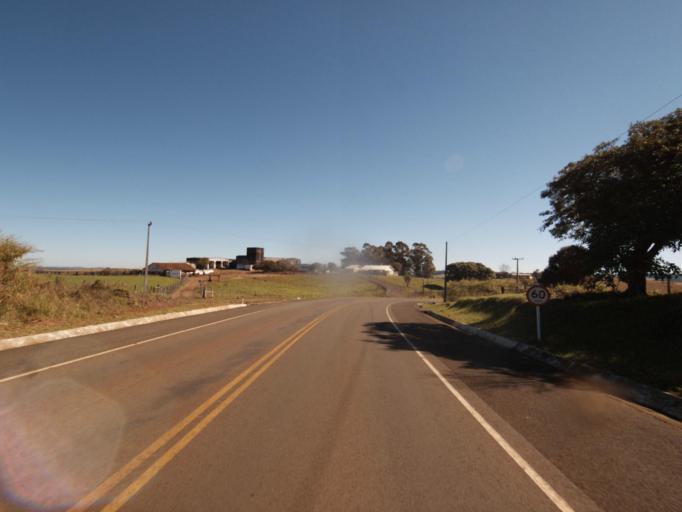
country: AR
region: Misiones
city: Bernardo de Irigoyen
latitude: -26.6699
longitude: -53.5972
